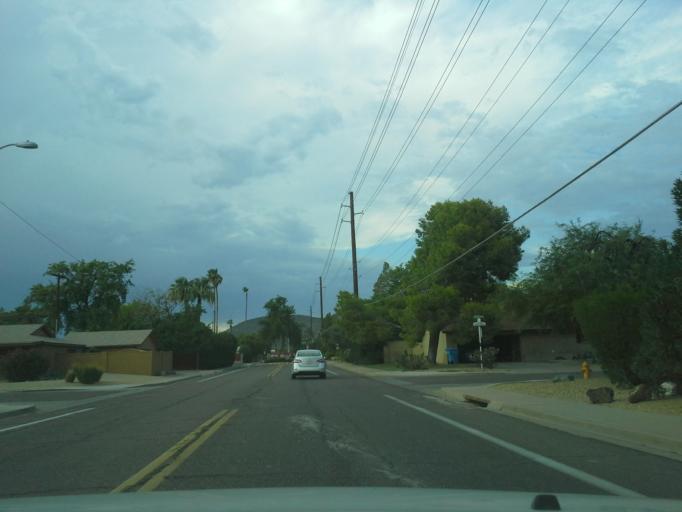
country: US
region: Arizona
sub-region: Maricopa County
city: Glendale
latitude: 33.5648
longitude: -112.0913
